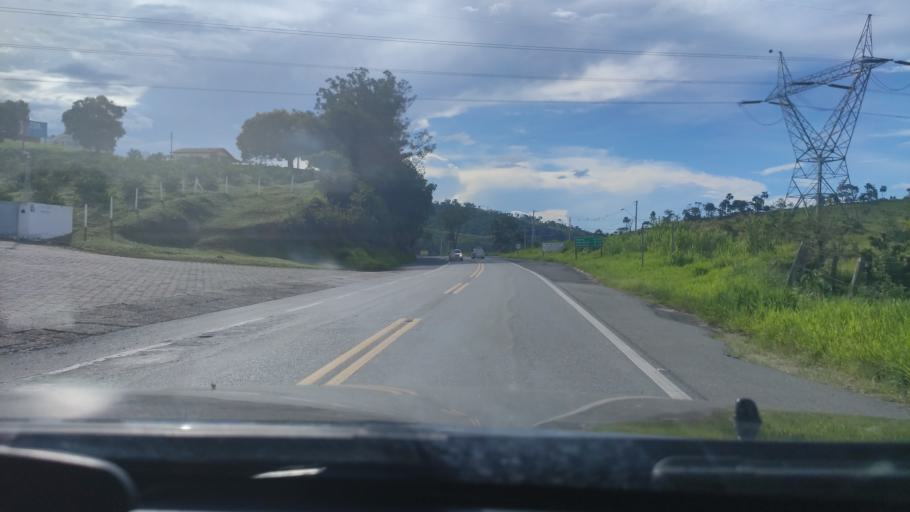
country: BR
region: Sao Paulo
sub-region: Aguas De Lindoia
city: Aguas de Lindoia
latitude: -22.5196
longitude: -46.6572
